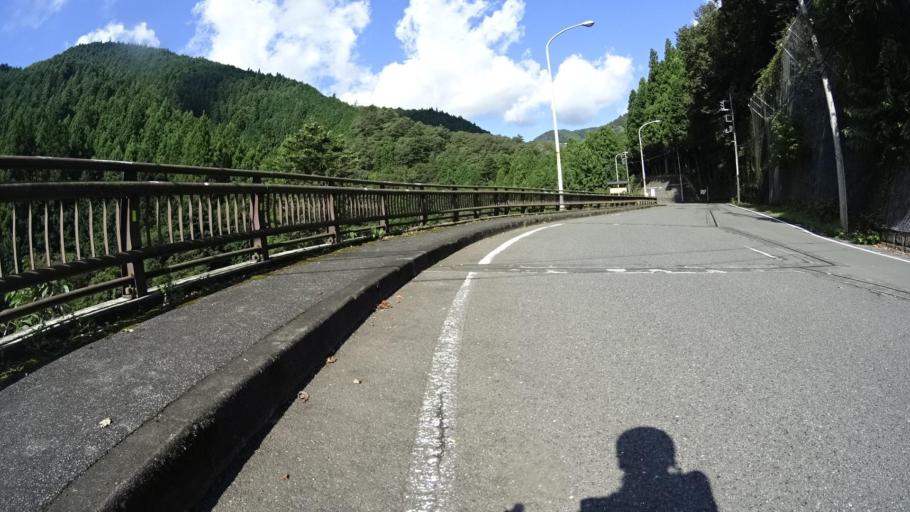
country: JP
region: Yamanashi
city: Uenohara
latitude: 35.7357
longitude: 139.0932
